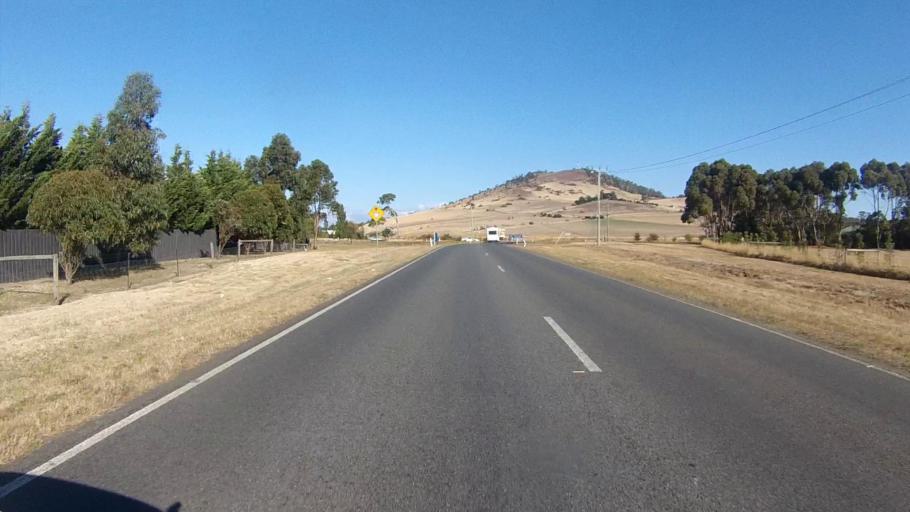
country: AU
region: Tasmania
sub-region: Clarence
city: Seven Mile Beach
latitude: -42.8598
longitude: 147.4929
